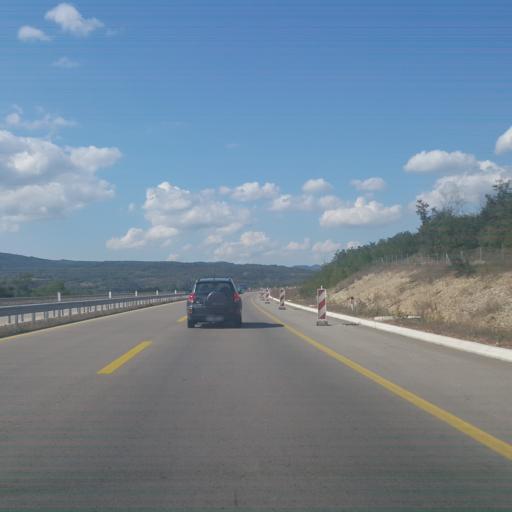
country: RS
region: Central Serbia
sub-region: Pirotski Okrug
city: Bela Palanka
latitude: 43.2388
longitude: 22.2900
